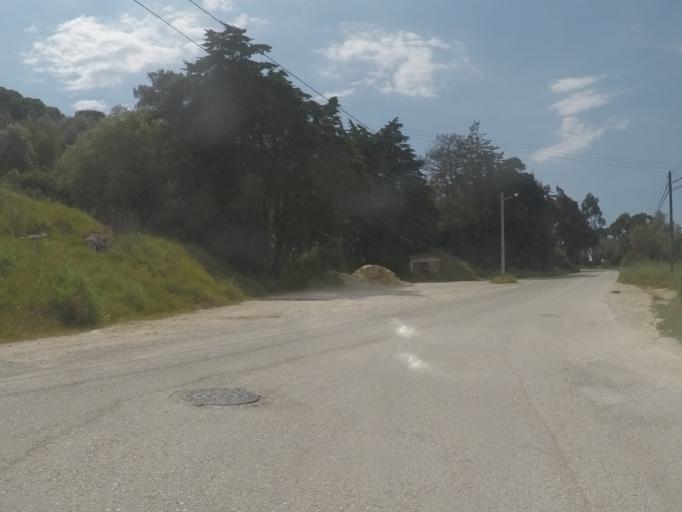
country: PT
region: Setubal
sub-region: Sesimbra
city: Sesimbra
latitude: 38.4638
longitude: -9.0927
